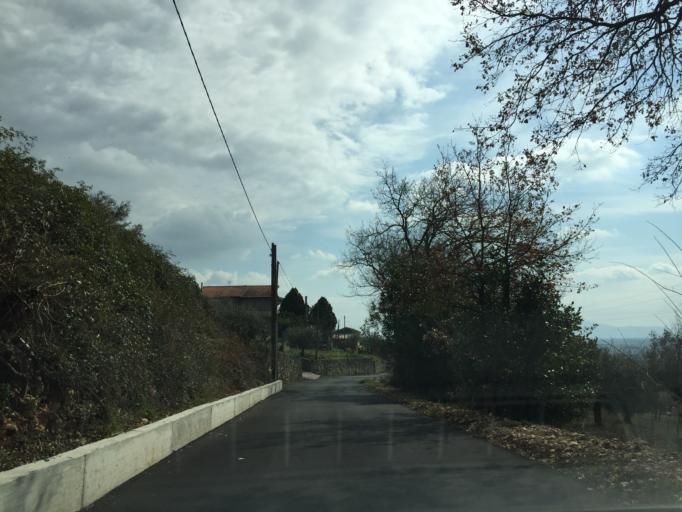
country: IT
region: Latium
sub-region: Provincia di Frosinone
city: Castrocielo
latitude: 41.5227
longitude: 13.7048
